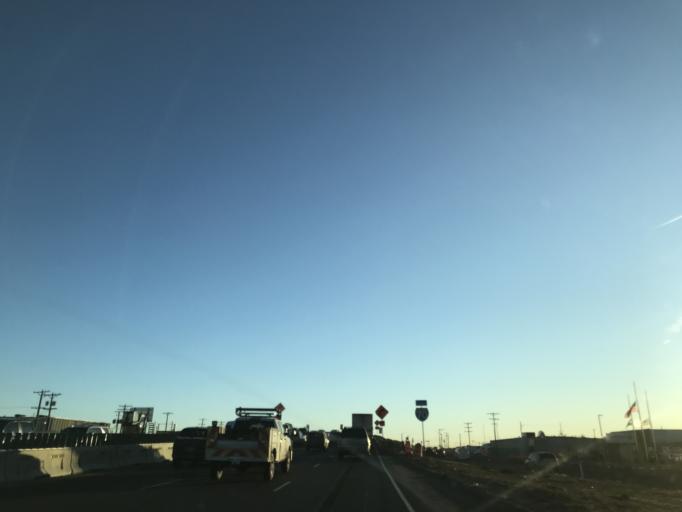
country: US
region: Colorado
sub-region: Adams County
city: Commerce City
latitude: 39.7800
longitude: -104.9354
